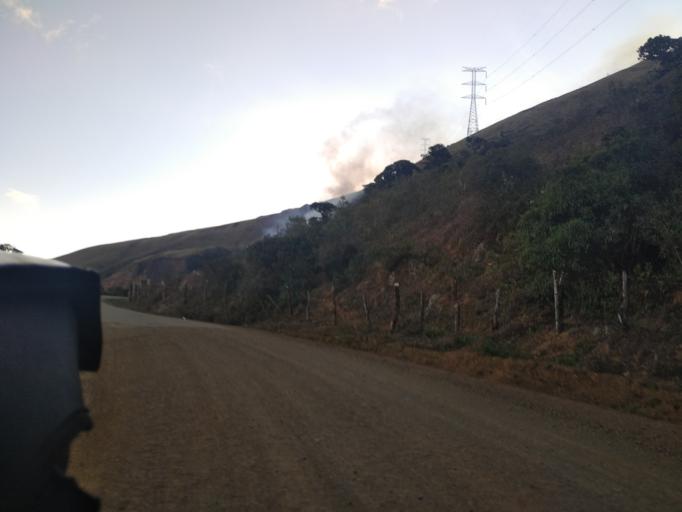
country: PE
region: Amazonas
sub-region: Provincia de Chachapoyas
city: Montevideo
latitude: -6.7191
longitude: -77.8748
